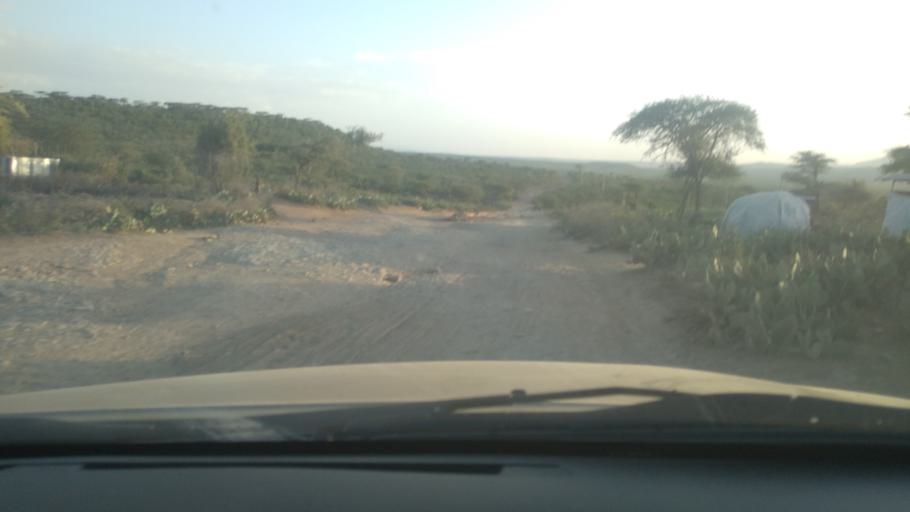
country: ET
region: Oromiya
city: Asbe Teferi
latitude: 9.2704
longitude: 40.8079
